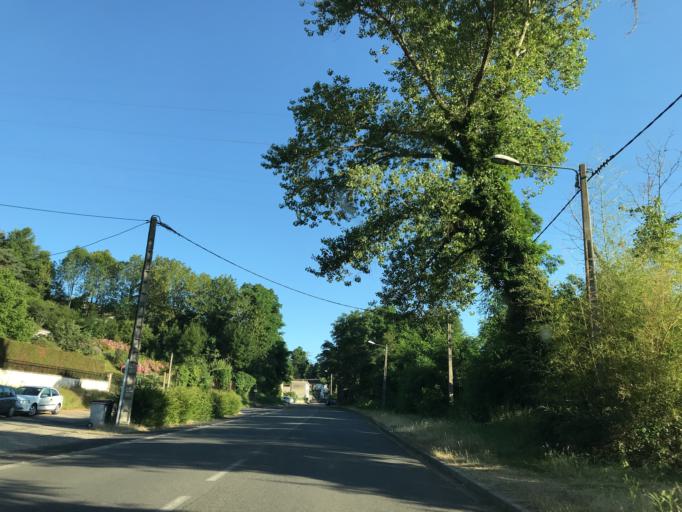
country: FR
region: Auvergne
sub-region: Departement du Puy-de-Dome
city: Thiers
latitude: 45.8703
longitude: 3.5311
